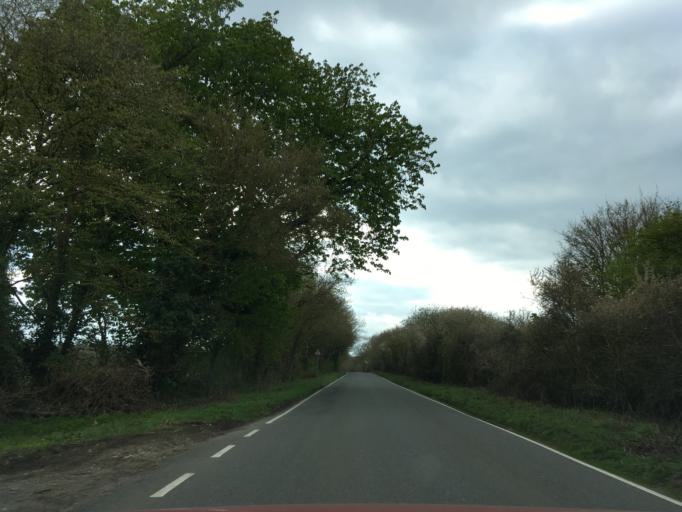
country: GB
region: England
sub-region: Oxfordshire
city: Kidlington
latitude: 51.8828
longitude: -1.2402
